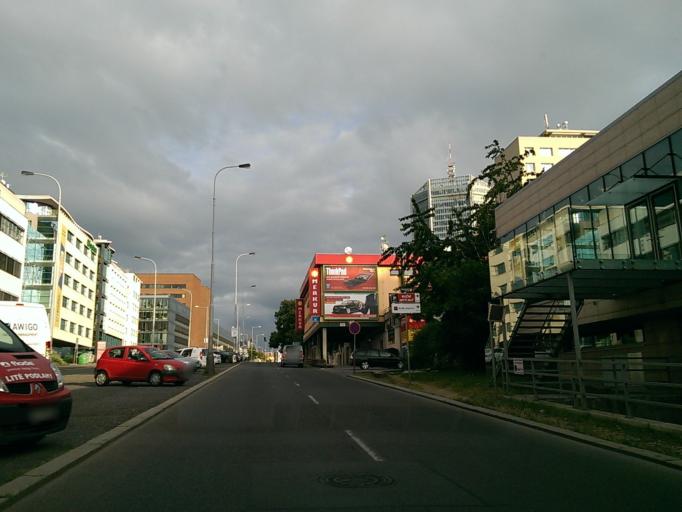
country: CZ
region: Praha
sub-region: Praha 2
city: Vysehrad
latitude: 50.0534
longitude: 14.4376
